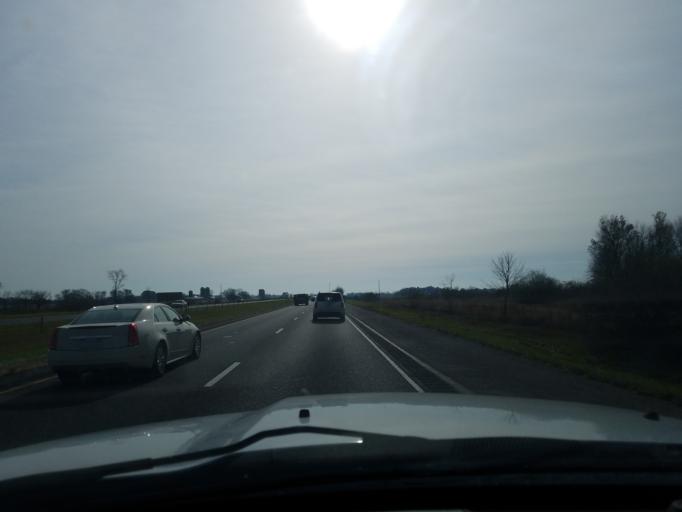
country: US
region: Indiana
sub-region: Delaware County
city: Yorktown
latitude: 40.2029
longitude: -85.5611
